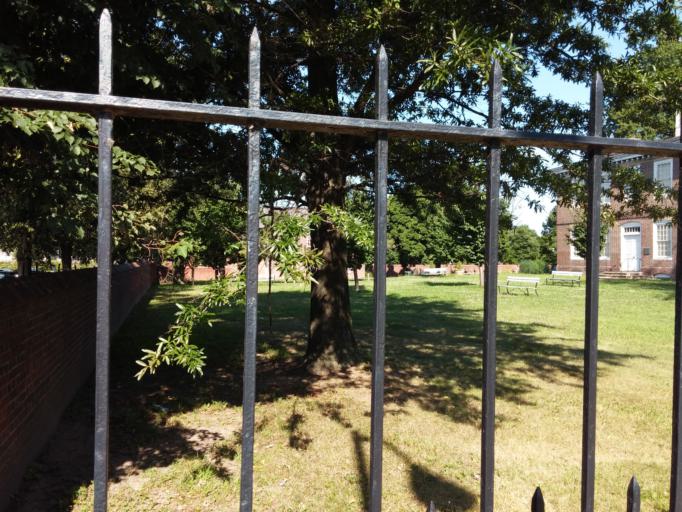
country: US
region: Pennsylvania
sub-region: Bucks County
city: Morrisville
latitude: 40.2128
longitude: -74.7653
